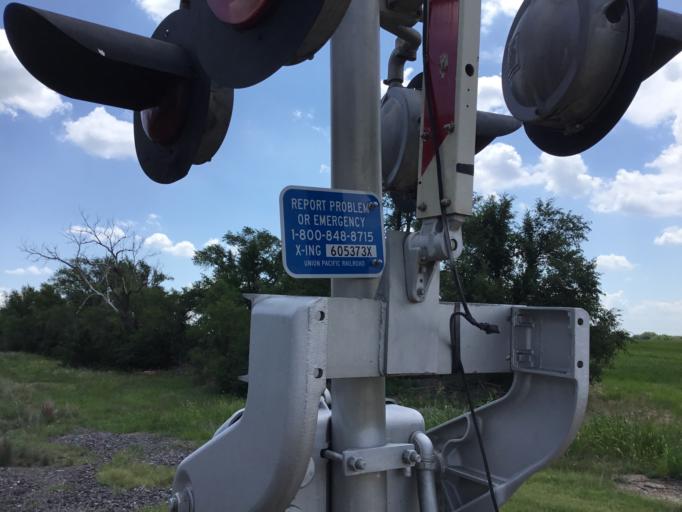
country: US
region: Kansas
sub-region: Pratt County
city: Pratt
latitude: 37.6438
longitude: -98.7666
